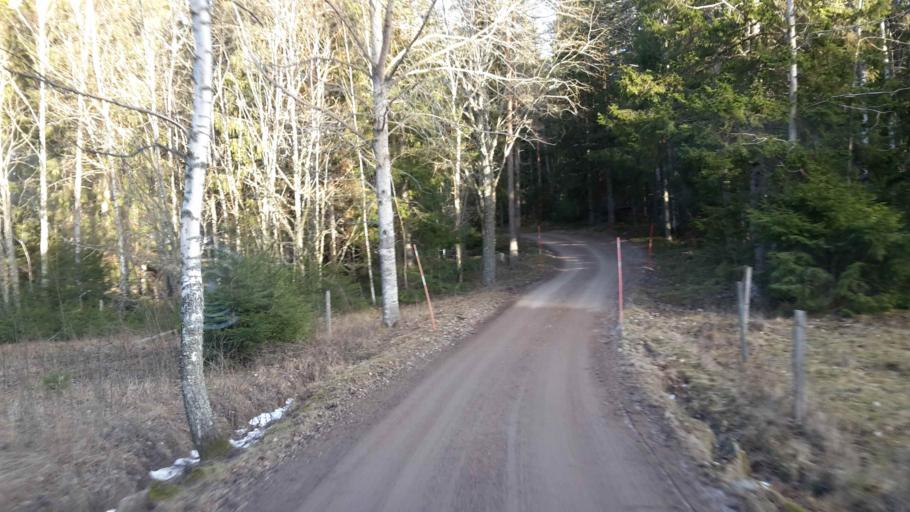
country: SE
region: OEstergoetland
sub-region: Atvidabergs Kommun
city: Atvidaberg
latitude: 58.2796
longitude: 15.9671
